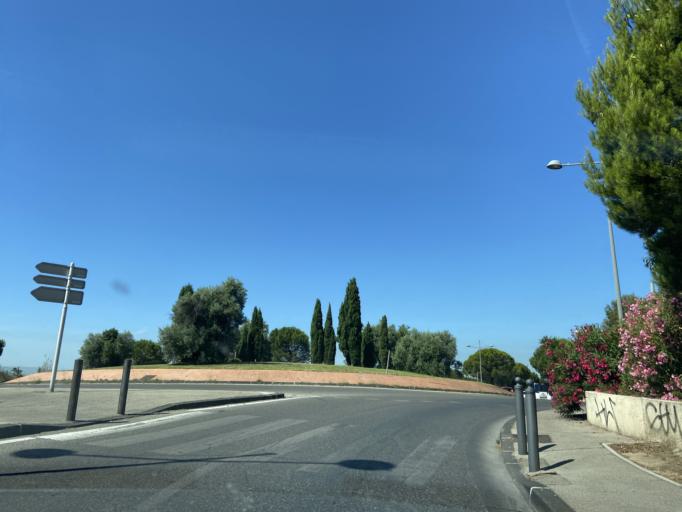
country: FR
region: Provence-Alpes-Cote d'Azur
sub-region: Departement des Bouches-du-Rhone
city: Marseille 15
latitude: 43.3662
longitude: 5.3551
